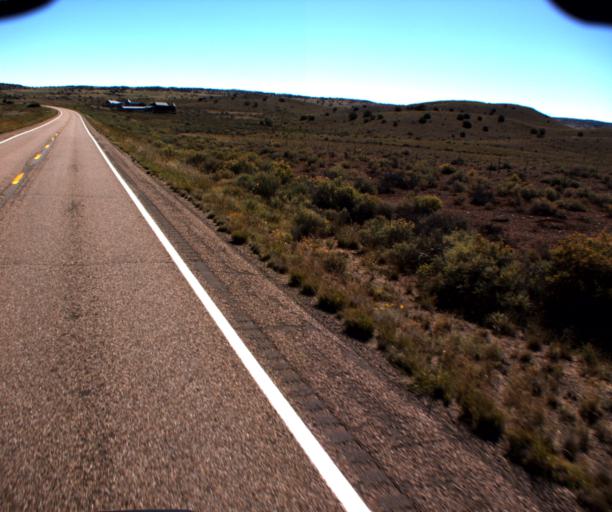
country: US
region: Arizona
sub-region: Apache County
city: Saint Johns
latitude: 34.5864
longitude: -109.5828
